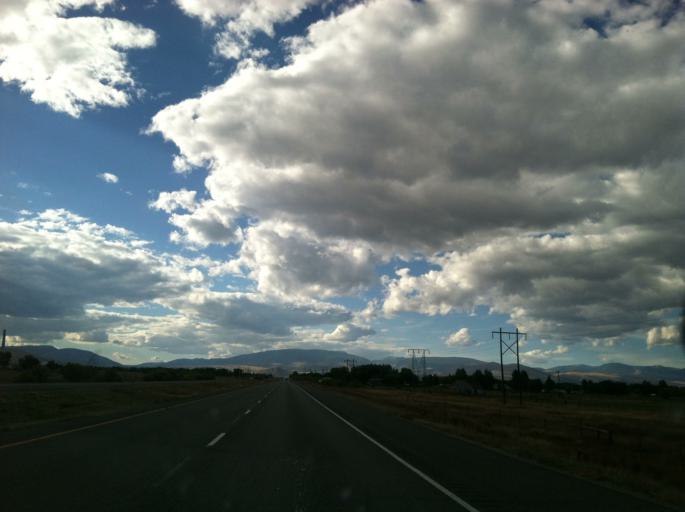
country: US
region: Montana
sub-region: Deer Lodge County
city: Warm Springs
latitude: 46.0986
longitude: -112.8306
